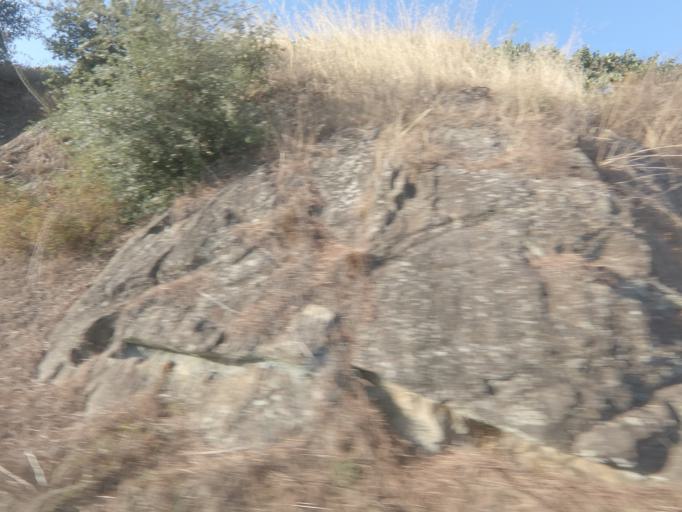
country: PT
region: Vila Real
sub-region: Sabrosa
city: Sabrosa
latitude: 41.2659
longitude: -7.5415
